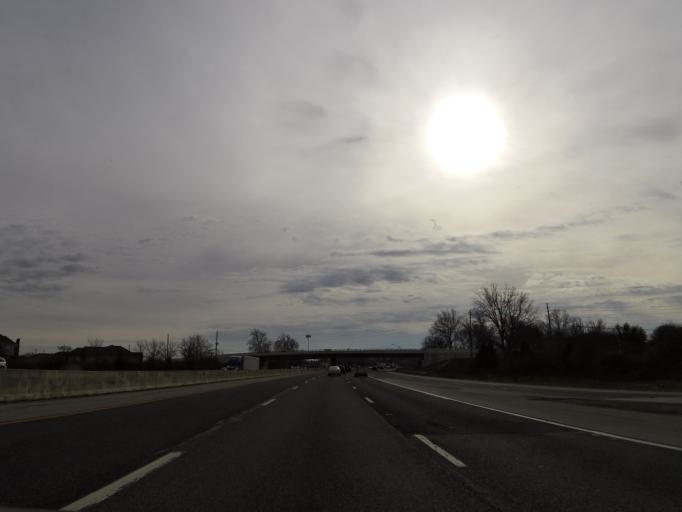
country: US
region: Indiana
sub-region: Marion County
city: Lawrence
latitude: 39.8924
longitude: -86.0509
